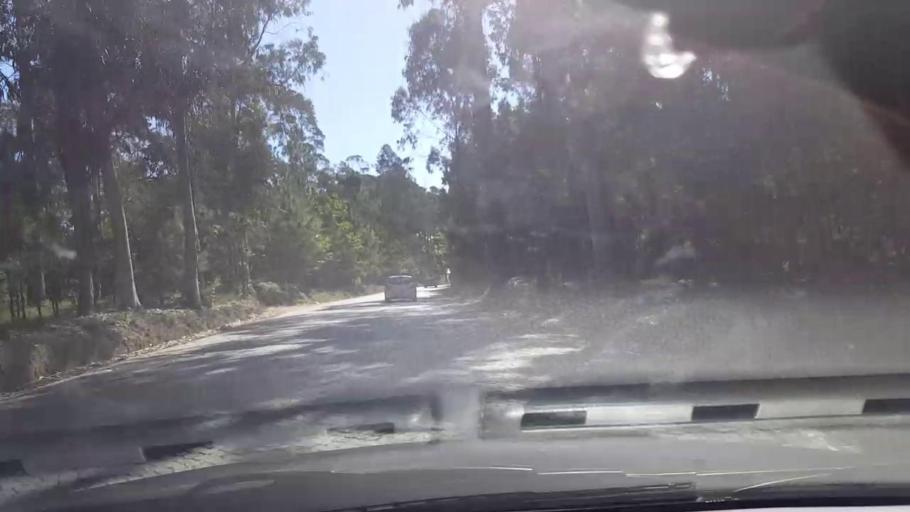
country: PT
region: Porto
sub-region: Vila do Conde
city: Arvore
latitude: 41.3236
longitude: -8.7251
